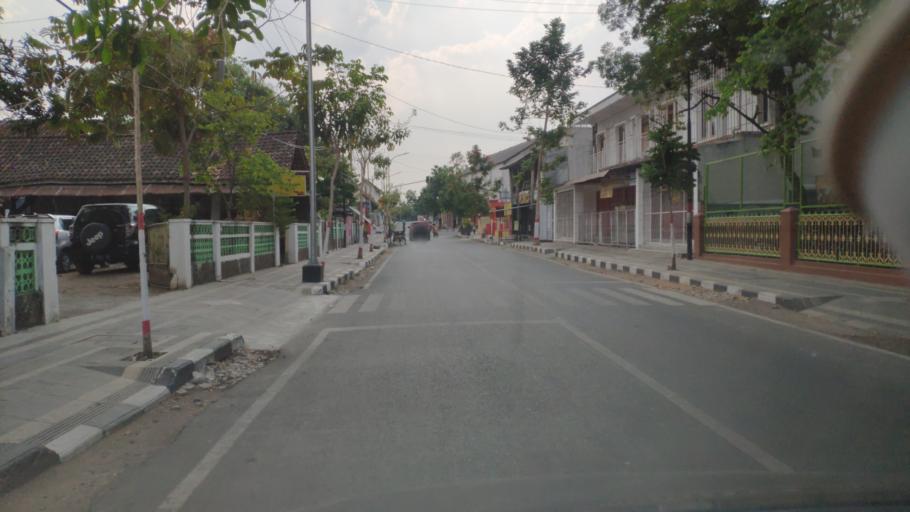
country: ID
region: Central Java
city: Tempelan
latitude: -6.9664
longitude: 111.4156
